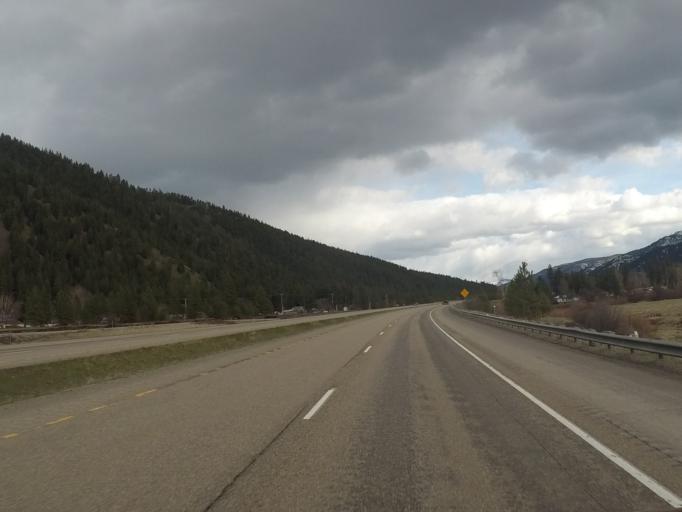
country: US
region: Montana
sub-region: Missoula County
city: Bonner-West Riverside
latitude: 46.8630
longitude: -113.8679
